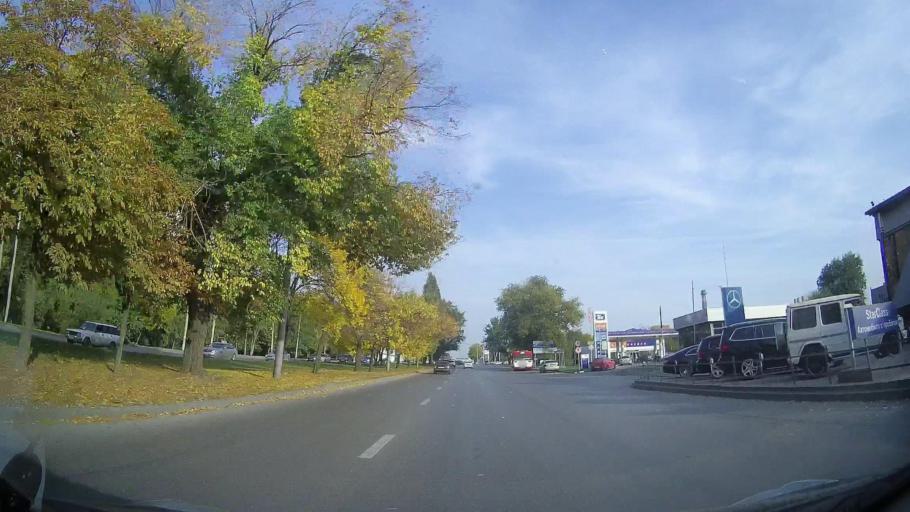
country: RU
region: Rostov
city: Imeni Chkalova
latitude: 47.2805
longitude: 39.7665
